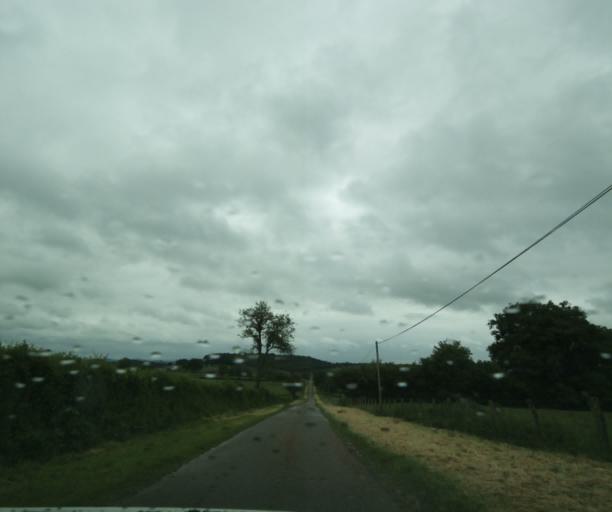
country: FR
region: Bourgogne
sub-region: Departement de Saone-et-Loire
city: Charolles
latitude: 46.4840
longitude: 4.2722
